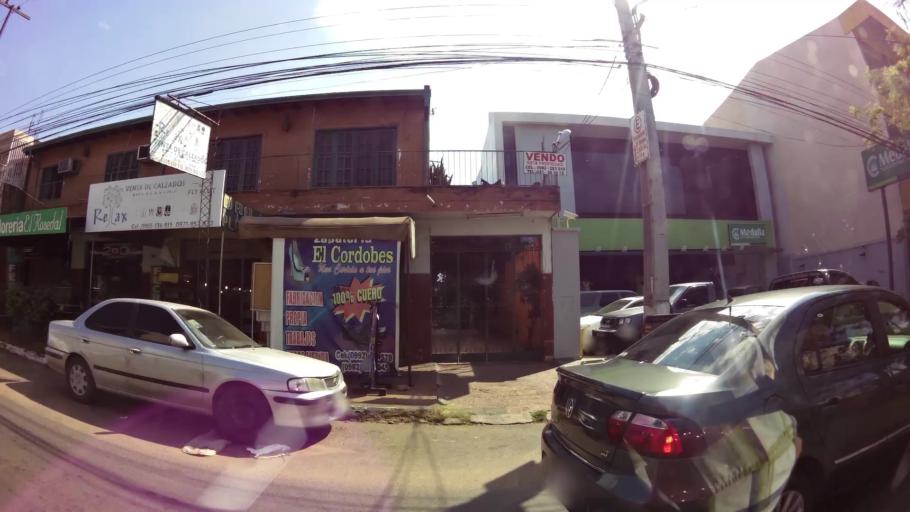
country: PY
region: Central
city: San Lorenzo
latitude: -25.3481
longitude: -57.5123
